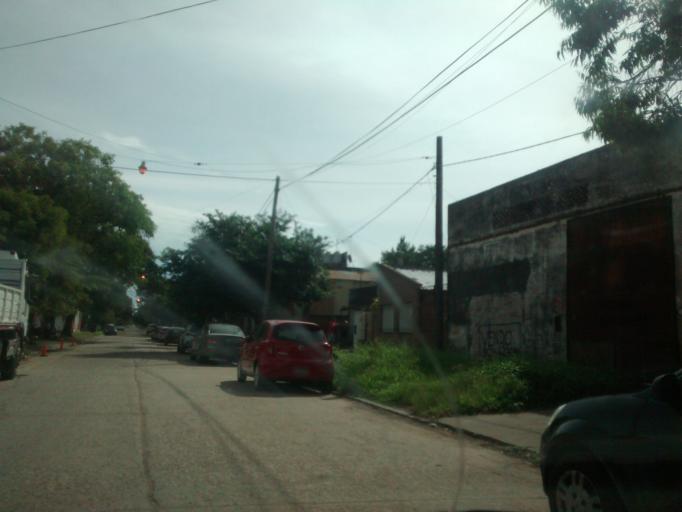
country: AR
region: Chaco
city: Fontana
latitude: -27.4370
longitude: -59.0030
